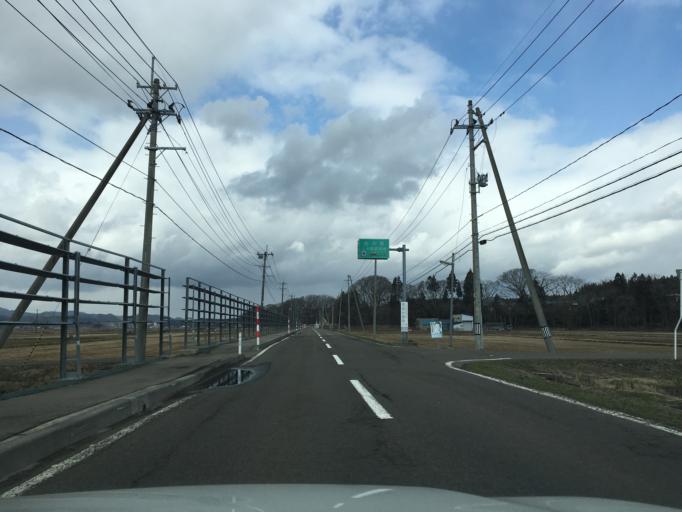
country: JP
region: Akita
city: Takanosu
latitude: 40.1403
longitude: 140.3505
